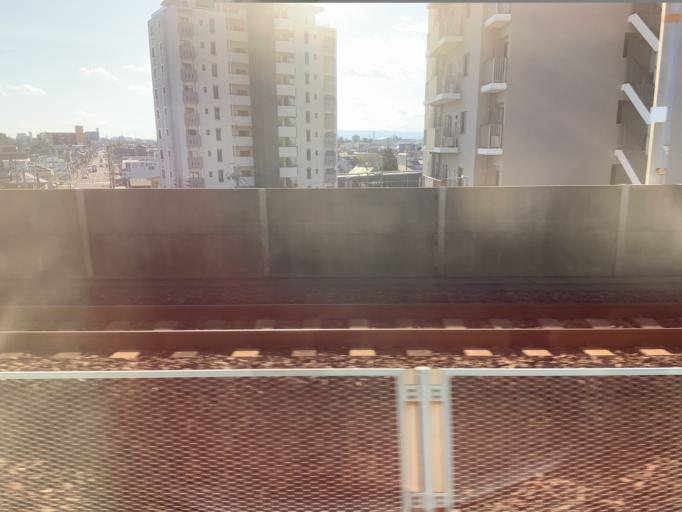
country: JP
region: Gifu
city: Gifu-shi
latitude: 35.4080
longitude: 136.7671
